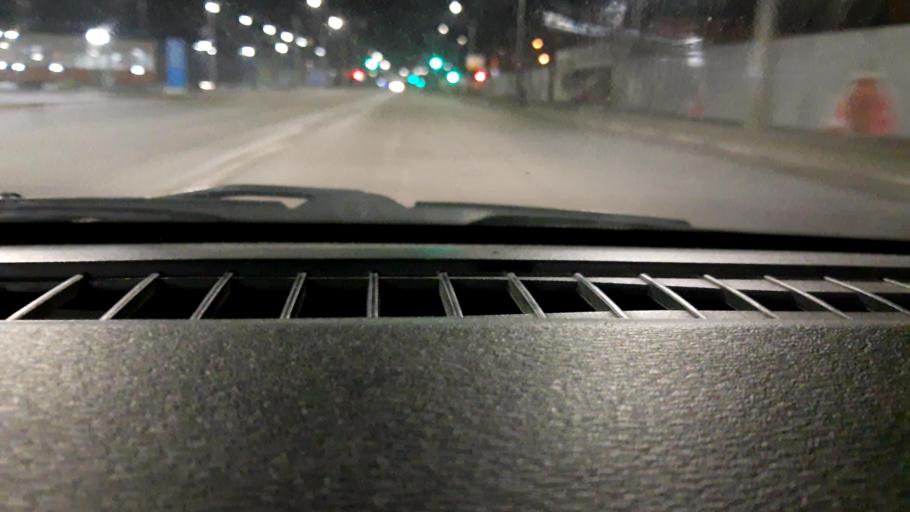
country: RU
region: Nizjnij Novgorod
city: Nizhniy Novgorod
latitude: 56.3372
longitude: 43.9481
